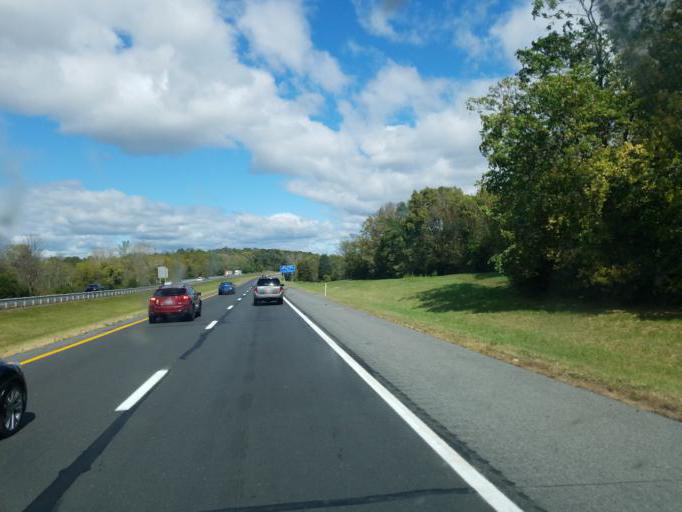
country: US
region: West Virginia
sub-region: Berkeley County
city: Inwood
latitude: 39.3048
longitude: -78.0788
